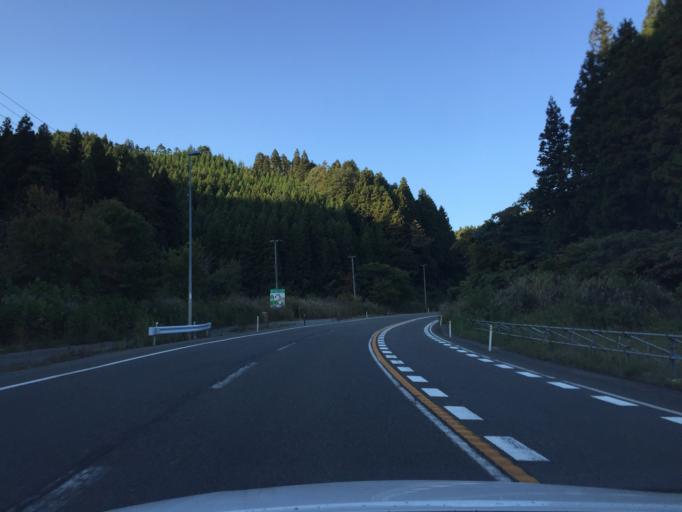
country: JP
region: Fukushima
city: Ishikawa
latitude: 37.1628
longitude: 140.6572
